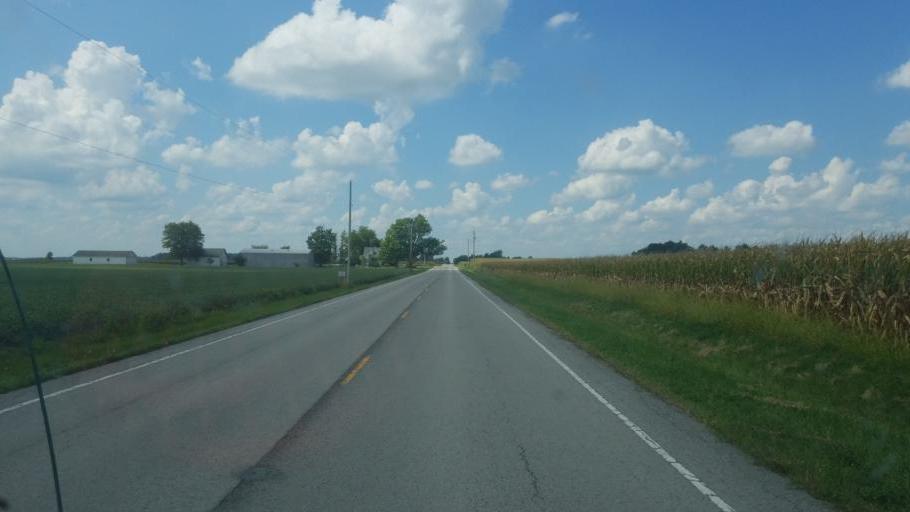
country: US
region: Ohio
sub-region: Hancock County
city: Arlington
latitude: 40.8340
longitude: -83.7182
